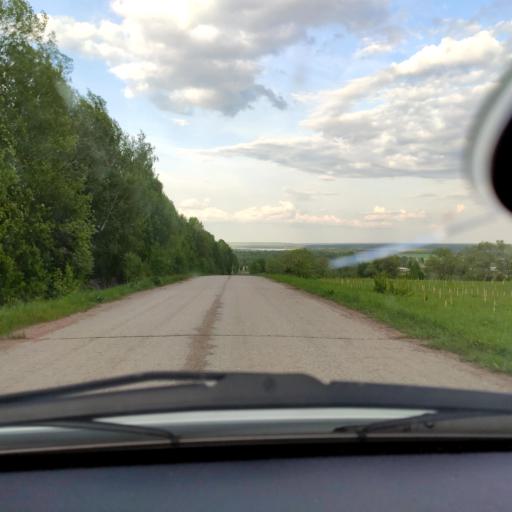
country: RU
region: Bashkortostan
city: Dyurtyuli
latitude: 55.5920
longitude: 54.9453
